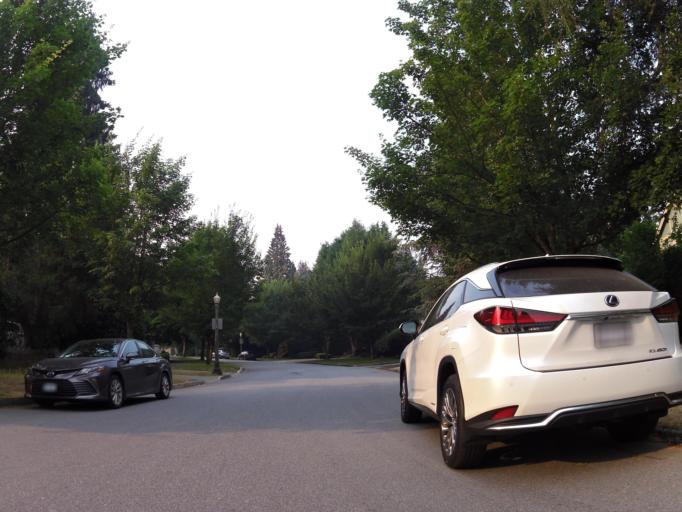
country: CA
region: British Columbia
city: Vancouver
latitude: 49.2380
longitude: -123.1470
